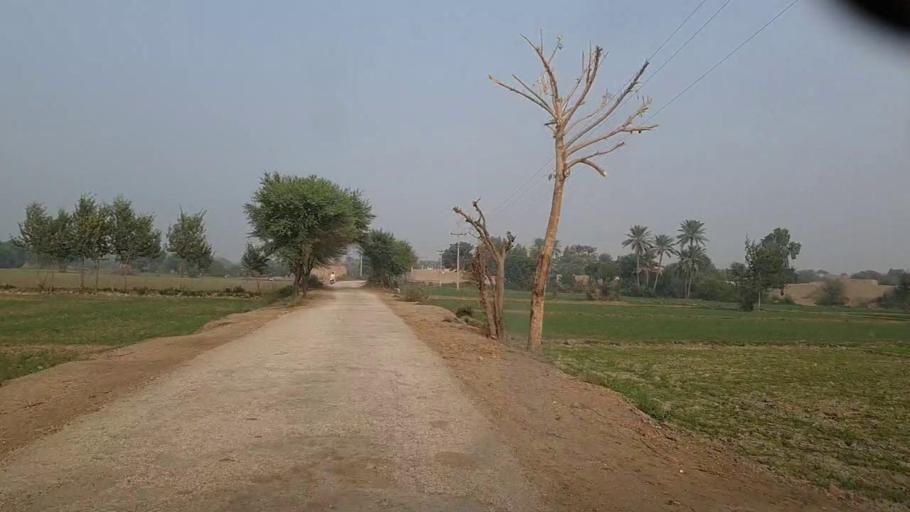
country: PK
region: Sindh
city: Bozdar
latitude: 27.1427
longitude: 68.6662
